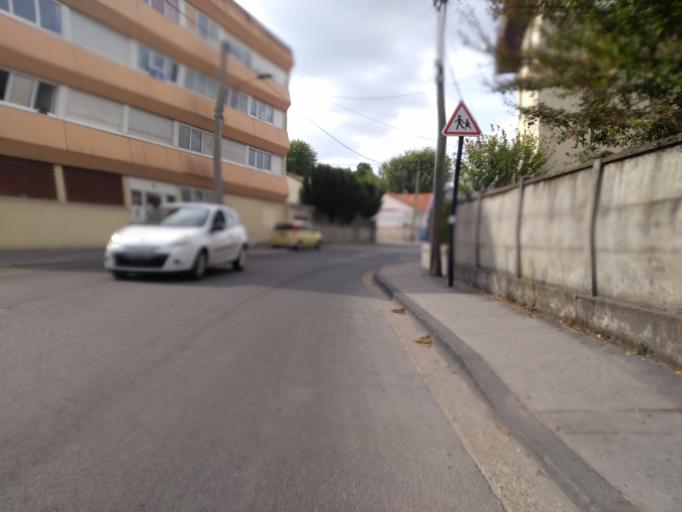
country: FR
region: Aquitaine
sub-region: Departement de la Gironde
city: Merignac
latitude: 44.8246
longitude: -0.6108
